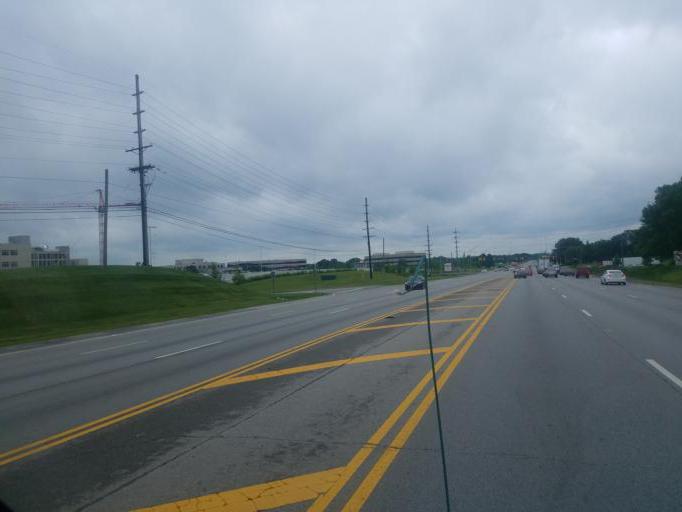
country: US
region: Ohio
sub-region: Franklin County
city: Reynoldsburg
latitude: 39.9797
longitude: -82.8409
